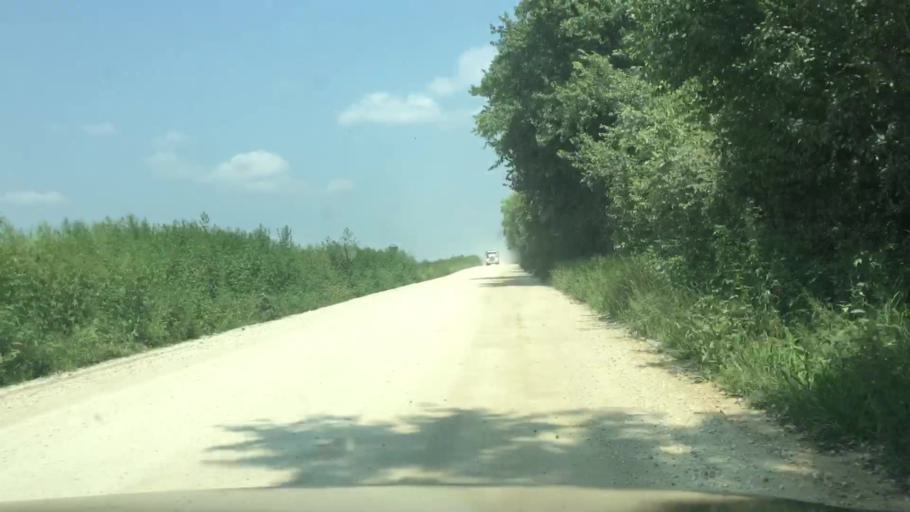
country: US
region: Kansas
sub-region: Allen County
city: Humboldt
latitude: 37.8253
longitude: -95.4093
